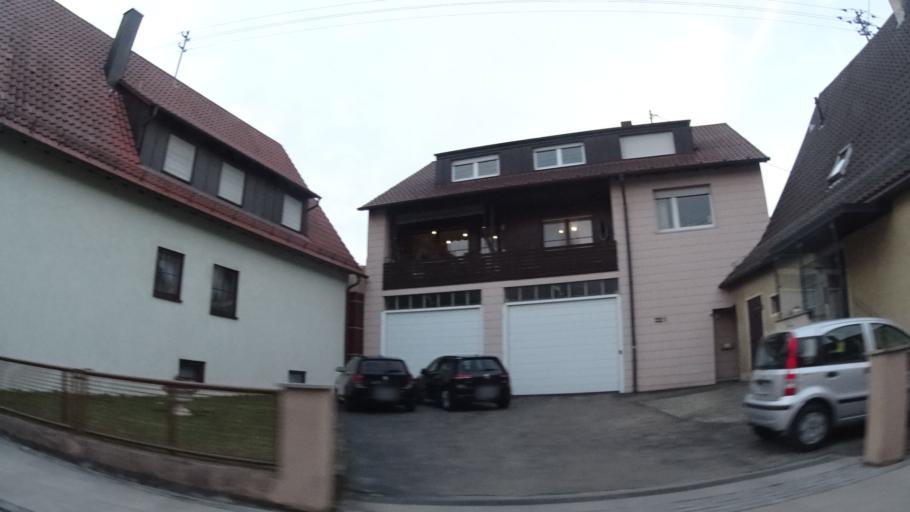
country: DE
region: Baden-Wuerttemberg
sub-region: Regierungsbezirk Stuttgart
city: Tamm
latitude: 48.9197
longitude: 9.1142
